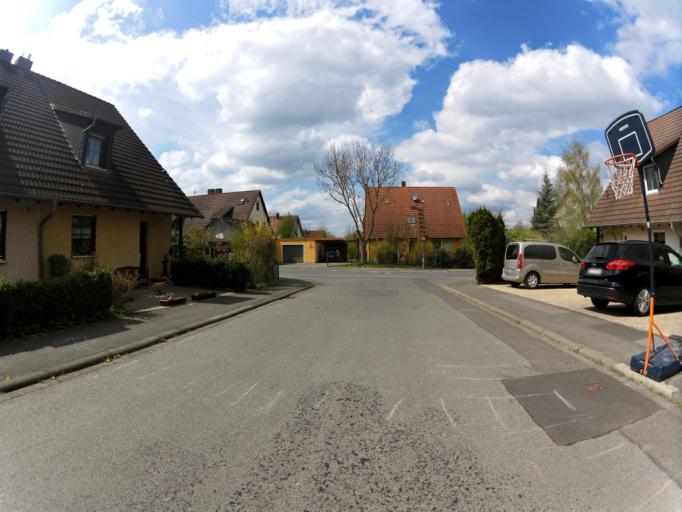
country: DE
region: Bavaria
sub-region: Regierungsbezirk Unterfranken
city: Giebelstadt
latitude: 49.6552
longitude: 9.9378
